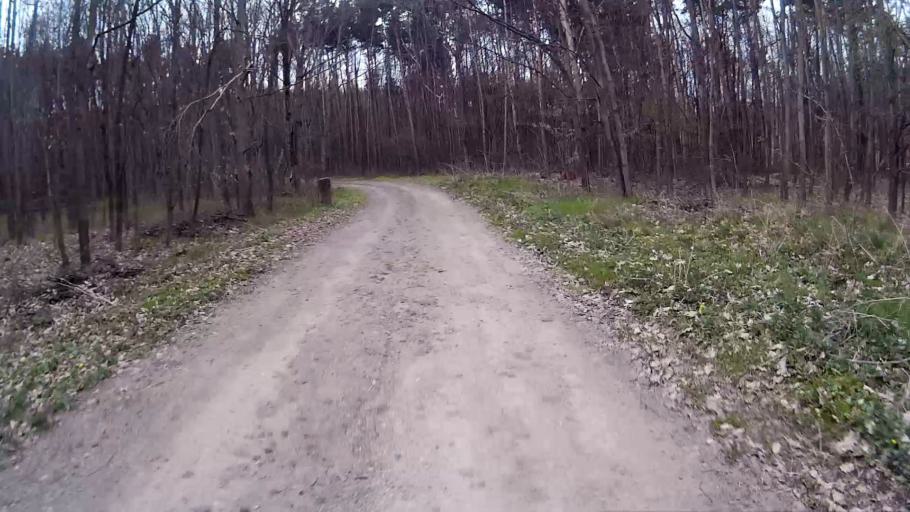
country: CZ
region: South Moravian
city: Ivancice
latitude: 49.0825
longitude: 16.4085
